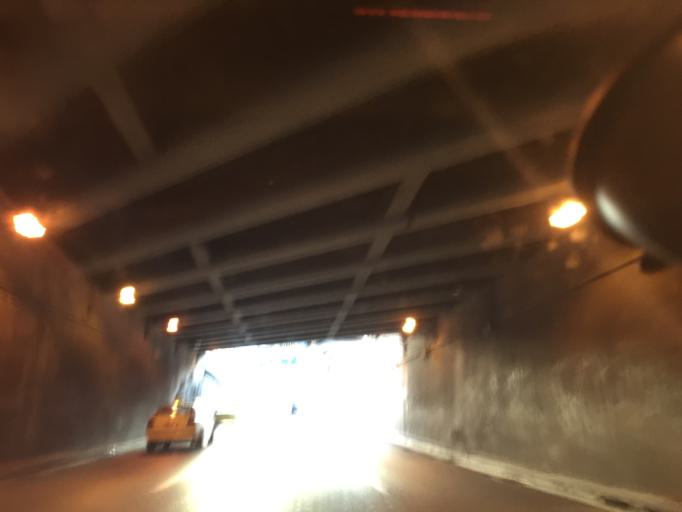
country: GR
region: Attica
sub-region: Nomarchia Athinas
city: Dhafni
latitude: 37.9615
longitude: 23.7228
